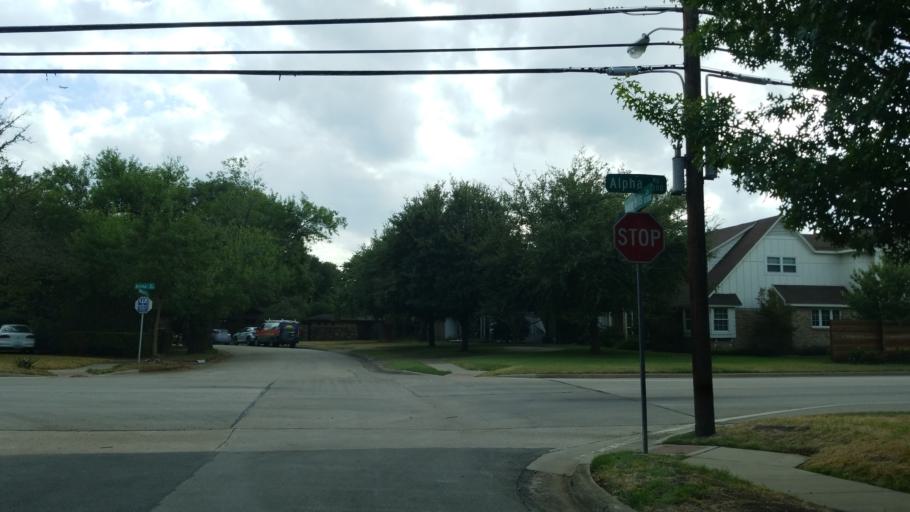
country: US
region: Texas
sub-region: Dallas County
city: Richardson
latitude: 32.9311
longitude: -96.7795
